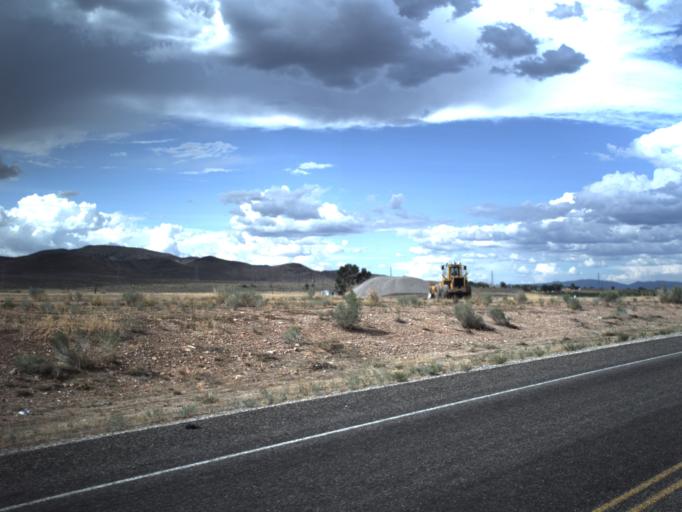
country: US
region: Utah
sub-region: Sevier County
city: Aurora
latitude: 38.8763
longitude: -111.9657
